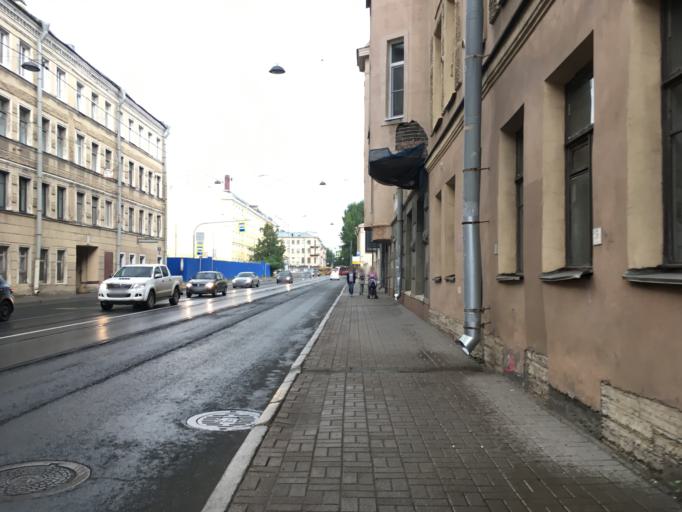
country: RU
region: St.-Petersburg
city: Centralniy
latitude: 59.9066
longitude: 30.3492
